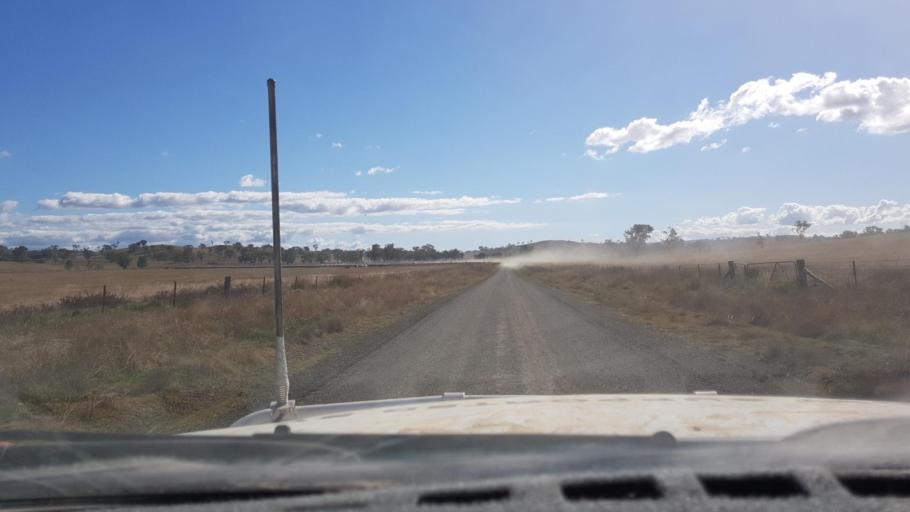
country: AU
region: New South Wales
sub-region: Narrabri
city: Blair Athol
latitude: -30.5120
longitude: 150.4445
